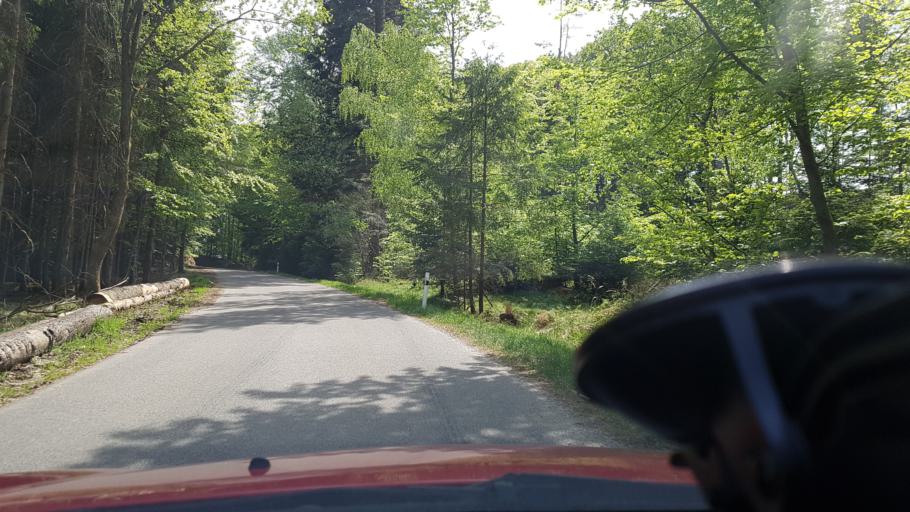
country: DE
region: Bavaria
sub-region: Lower Bavaria
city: Stubenberg
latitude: 48.3073
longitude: 13.1022
